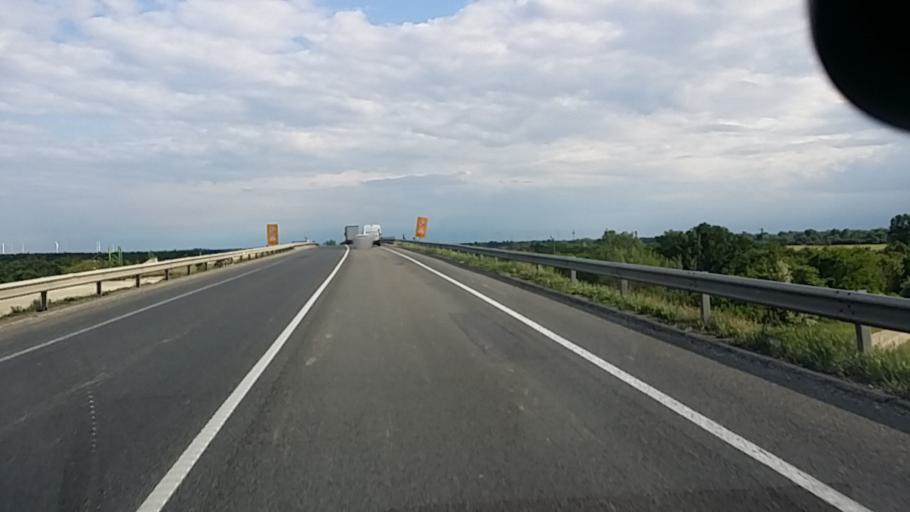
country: HU
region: Gyor-Moson-Sopron
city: Rajka
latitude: 47.9367
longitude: 17.1676
